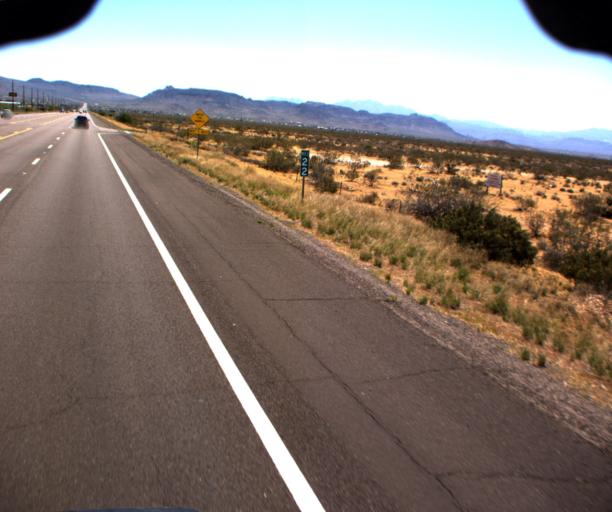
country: US
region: Arizona
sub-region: Mohave County
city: Golden Valley
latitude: 35.2219
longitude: -114.2149
